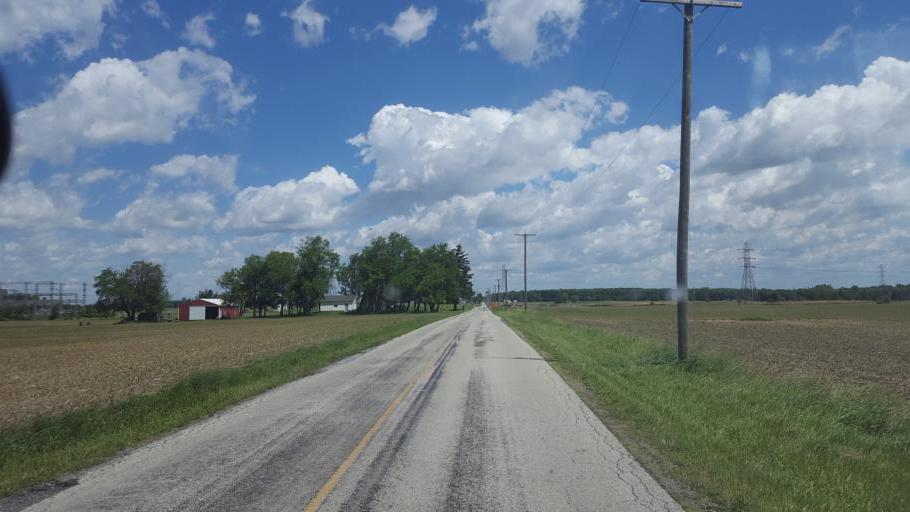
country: US
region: Ohio
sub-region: Richland County
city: Shelby
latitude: 40.8470
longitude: -82.6773
